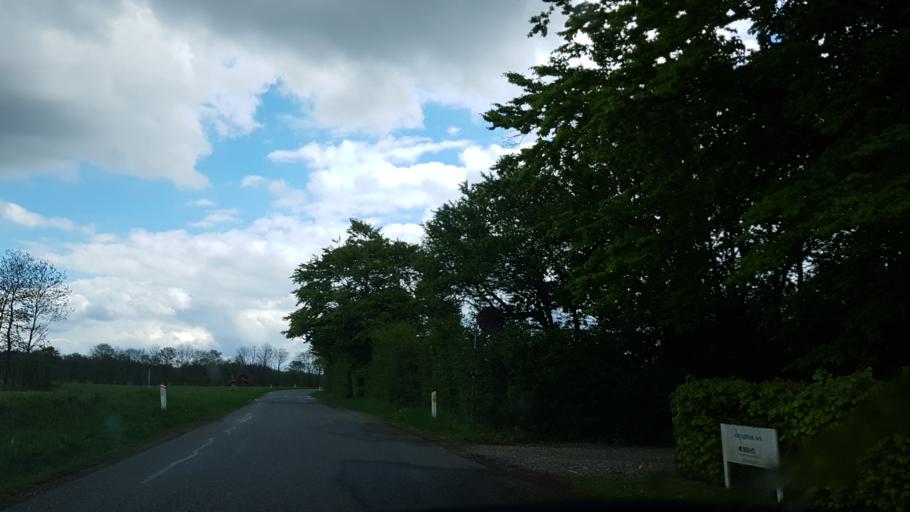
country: DK
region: South Denmark
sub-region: Haderslev Kommune
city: Vojens
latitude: 55.2217
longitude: 9.2935
